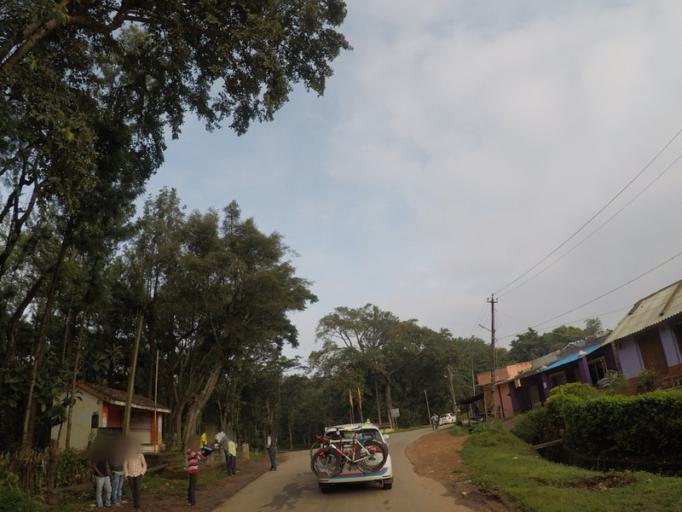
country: IN
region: Karnataka
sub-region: Chikmagalur
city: Chikmagalur
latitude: 13.4546
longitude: 75.7991
